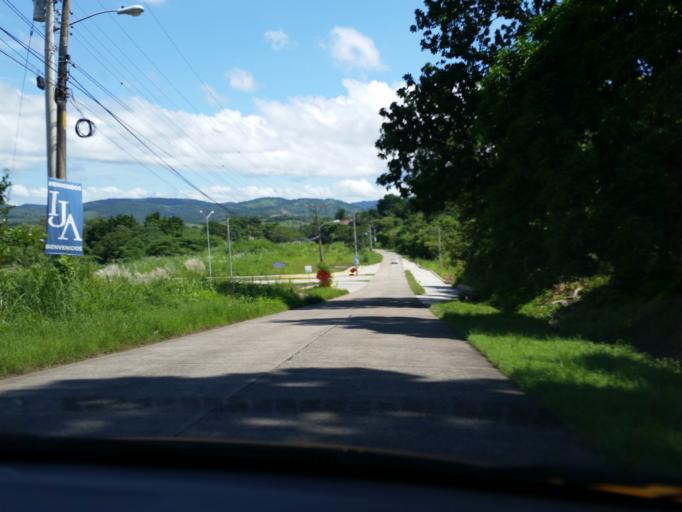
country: PA
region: Panama
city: San Miguelito
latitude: 9.0729
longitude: -79.4706
